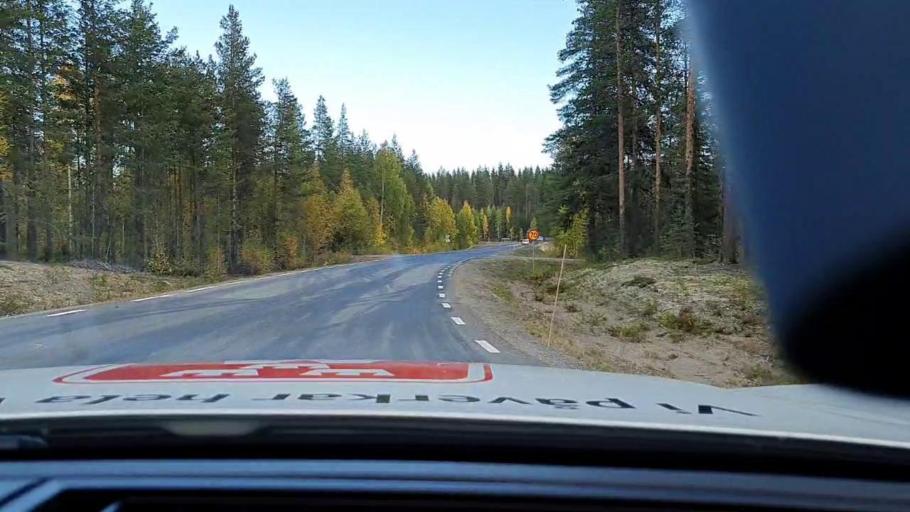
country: SE
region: Vaesterbotten
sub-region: Skelleftea Kommun
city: Langsele
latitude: 64.9611
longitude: 19.8856
